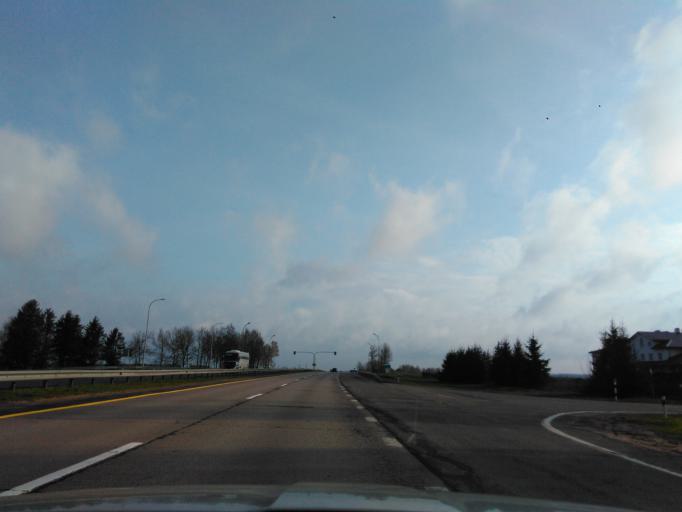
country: BY
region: Minsk
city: Lahoysk
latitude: 54.1666
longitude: 27.8177
